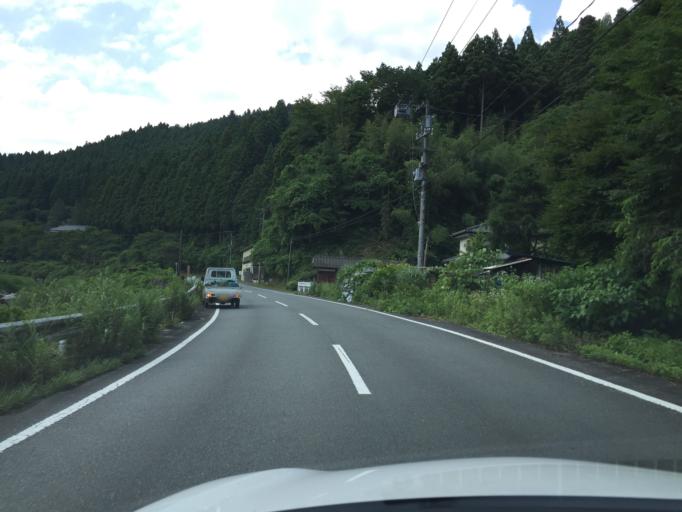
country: JP
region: Fukushima
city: Iwaki
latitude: 37.0071
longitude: 140.7190
